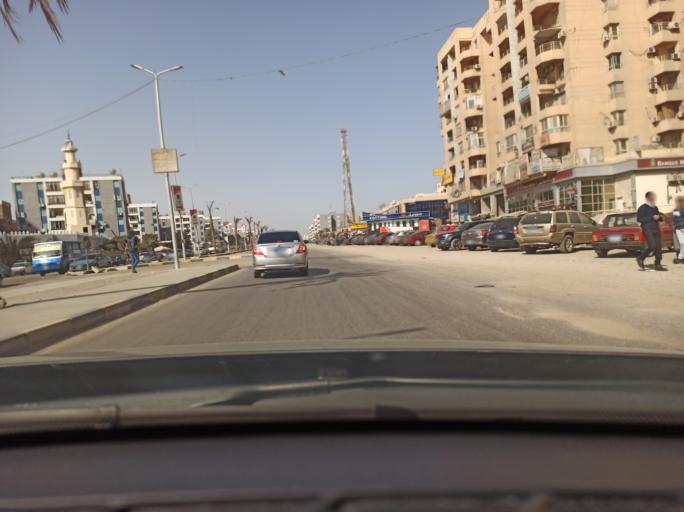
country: EG
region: Muhafazat al Qahirah
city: Cairo
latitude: 30.0509
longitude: 31.3957
